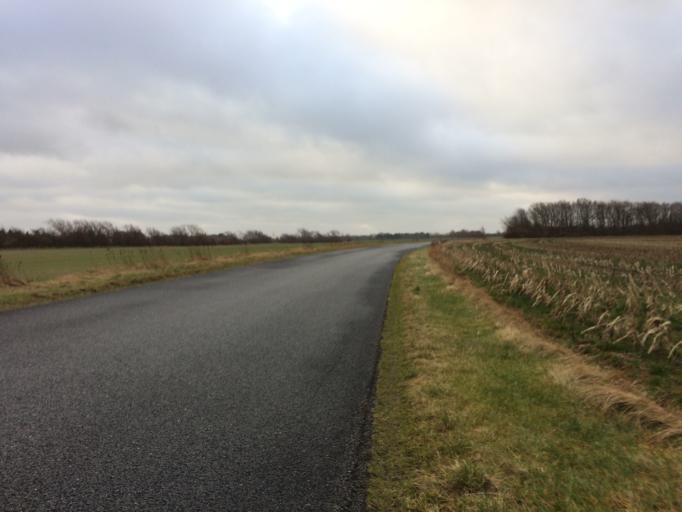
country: DK
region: Central Jutland
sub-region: Holstebro Kommune
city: Ulfborg
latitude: 56.2711
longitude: 8.2362
